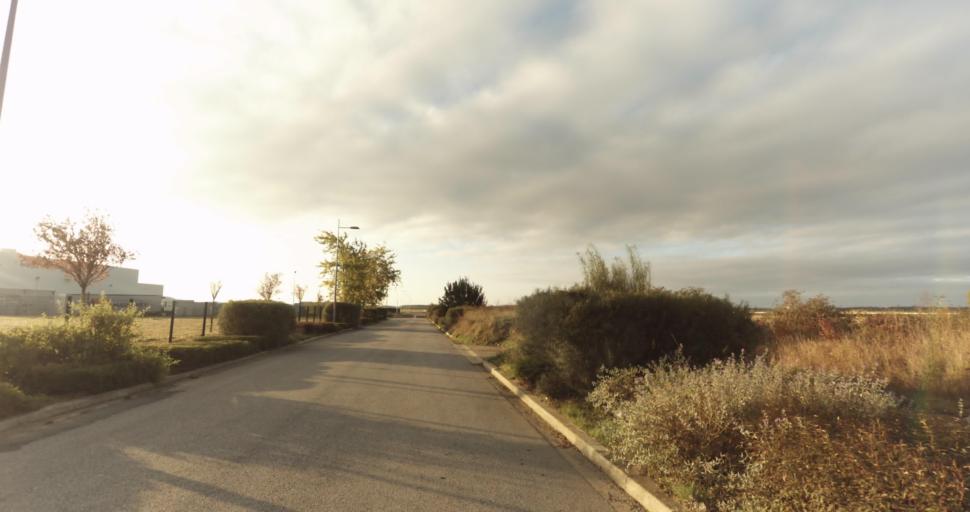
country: FR
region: Centre
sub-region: Departement d'Eure-et-Loir
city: Vernouillet
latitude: 48.7093
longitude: 1.3722
